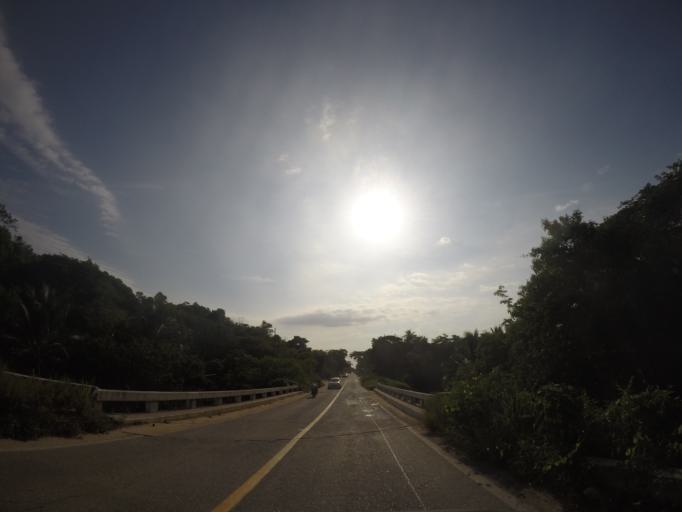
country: MX
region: Oaxaca
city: San Pedro Pochutla
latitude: 15.7320
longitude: -96.5034
